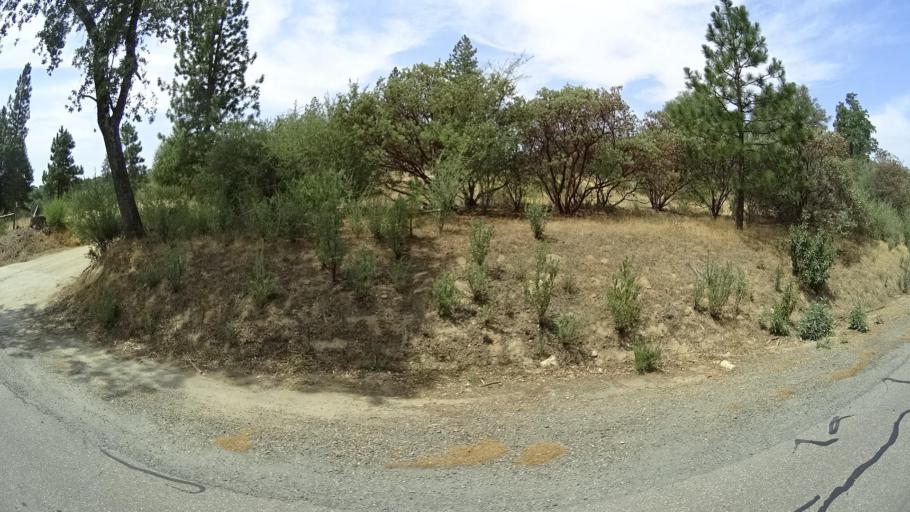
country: US
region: California
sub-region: Madera County
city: Ahwahnee
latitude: 37.4445
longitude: -119.8270
